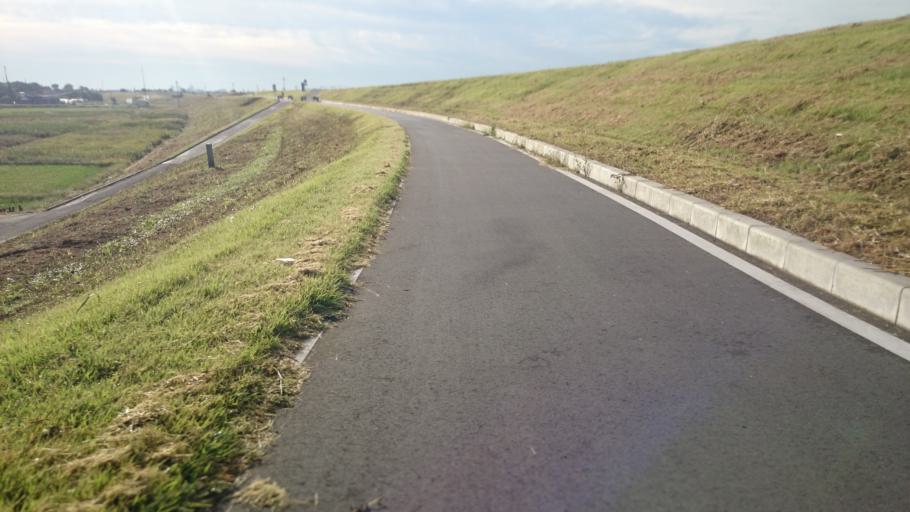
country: JP
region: Saitama
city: Kamifukuoka
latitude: 35.9077
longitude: 139.5598
